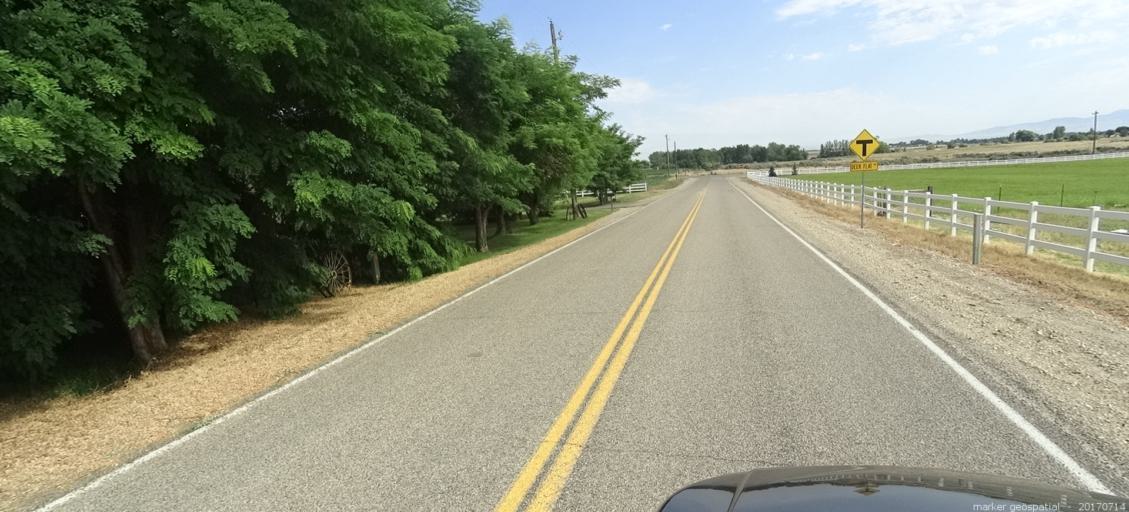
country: US
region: Idaho
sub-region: Ada County
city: Kuna
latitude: 43.5012
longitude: -116.3543
